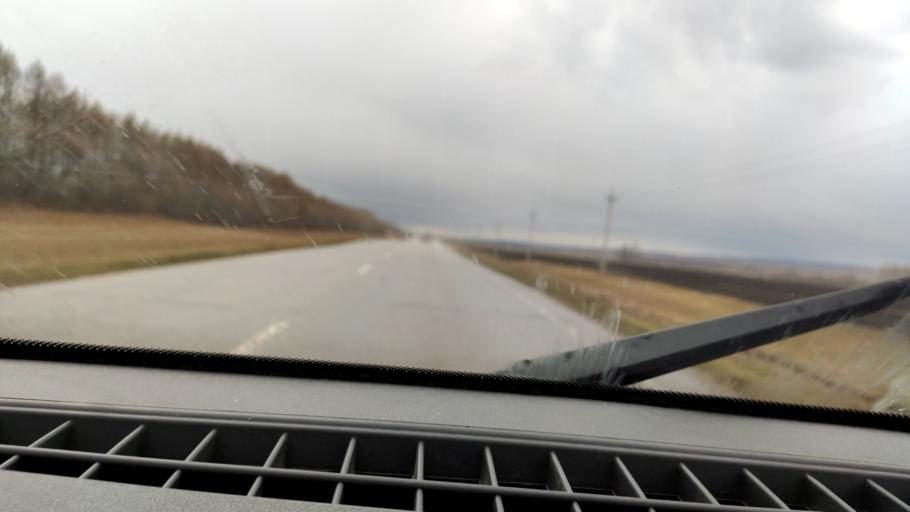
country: RU
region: Bashkortostan
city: Chekmagush
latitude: 55.1115
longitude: 54.9131
